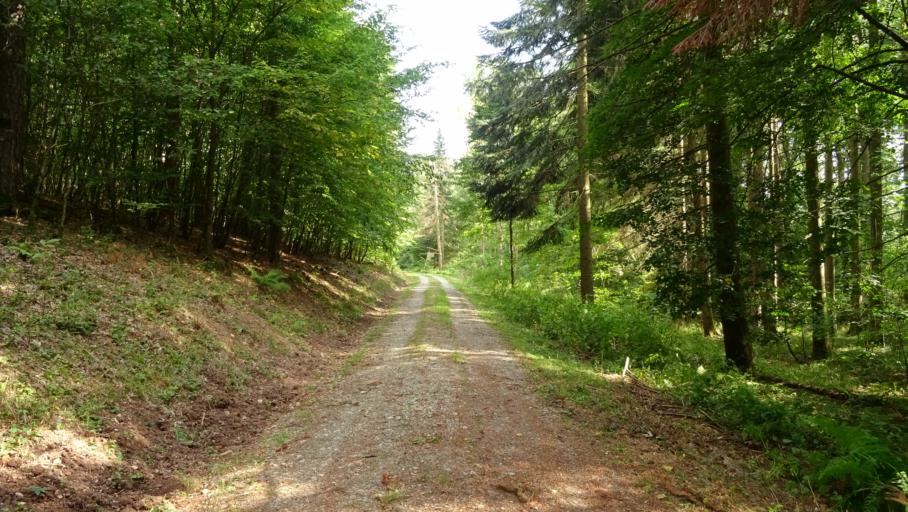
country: DE
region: Baden-Wuerttemberg
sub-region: Karlsruhe Region
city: Fahrenbach
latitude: 49.4108
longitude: 9.1261
